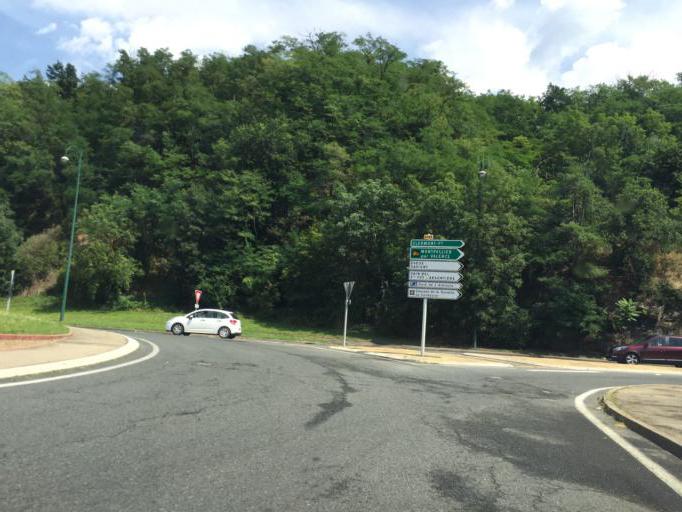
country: FR
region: Rhone-Alpes
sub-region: Departement du Rhone
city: Saint-Germain-Nuelles
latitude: 45.8376
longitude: 4.6216
